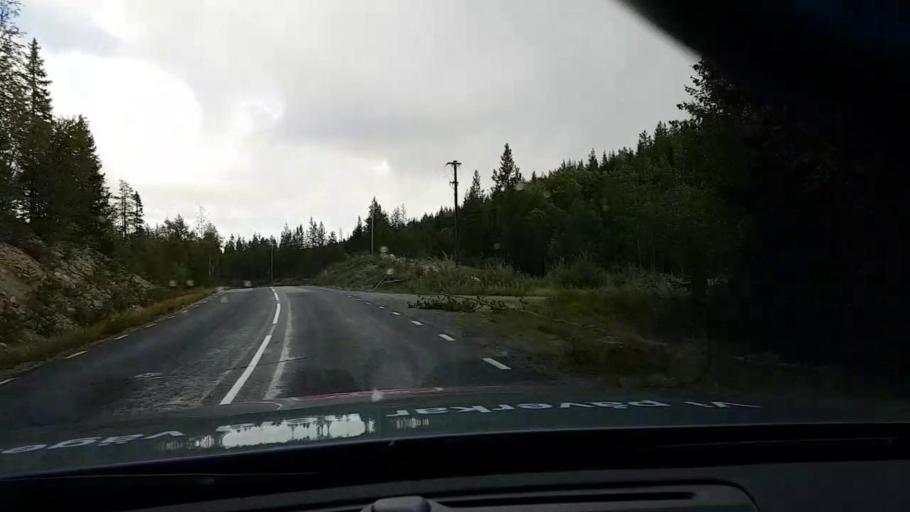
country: SE
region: Vaesterbotten
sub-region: Asele Kommun
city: Asele
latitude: 63.8308
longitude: 17.4538
